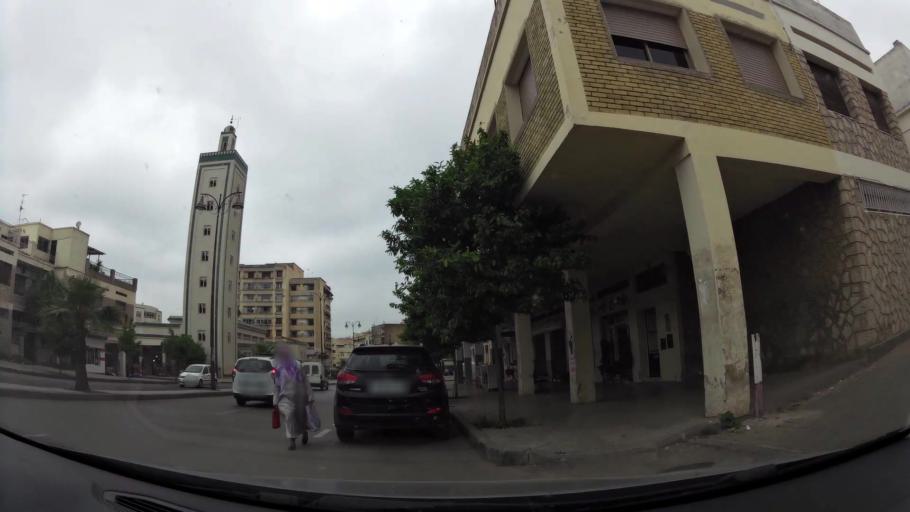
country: MA
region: Fes-Boulemane
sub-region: Fes
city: Fes
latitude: 34.0429
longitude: -5.0064
